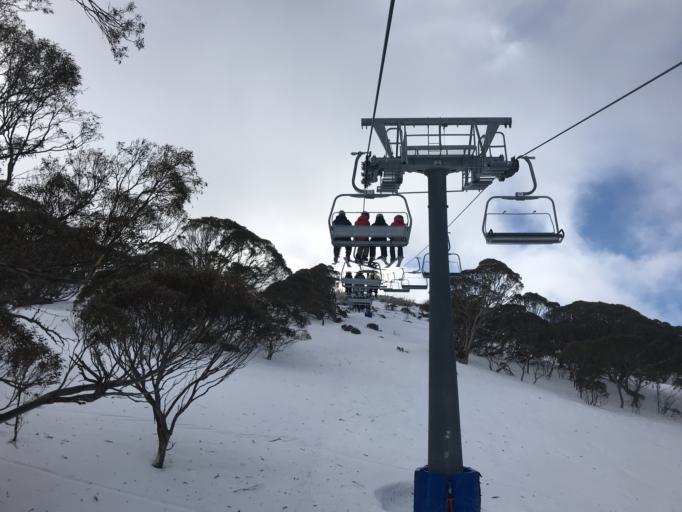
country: AU
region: New South Wales
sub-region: Snowy River
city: Jindabyne
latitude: -36.3844
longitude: 148.3803
